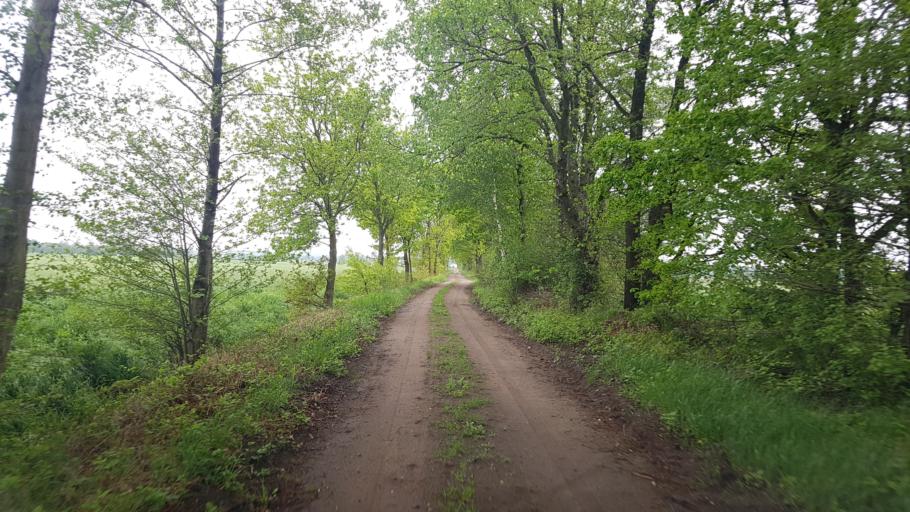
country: DE
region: Brandenburg
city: Elsterwerda
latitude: 51.4385
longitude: 13.5438
